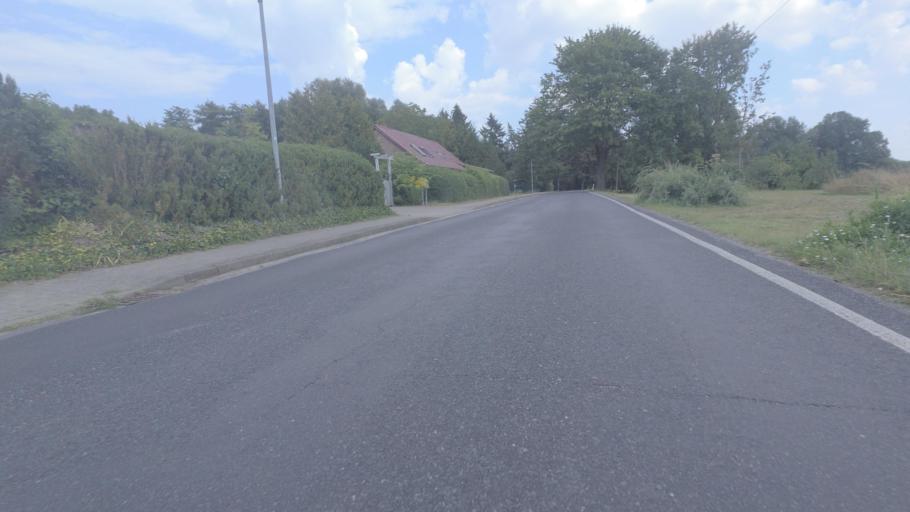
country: DE
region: Mecklenburg-Vorpommern
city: Borrentin
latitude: 53.8517
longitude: 12.9643
